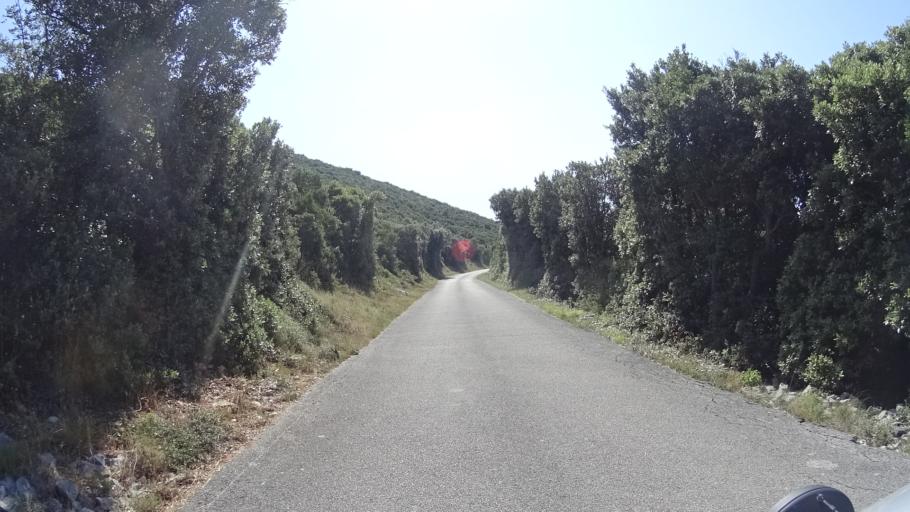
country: HR
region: Istarska
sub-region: Grad Labin
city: Rabac
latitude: 44.9777
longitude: 14.1312
